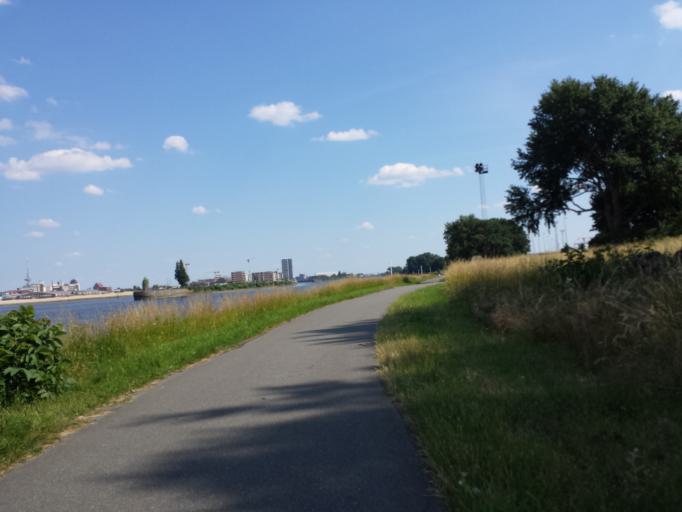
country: DE
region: Lower Saxony
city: Ritterhude
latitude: 53.1088
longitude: 8.7410
